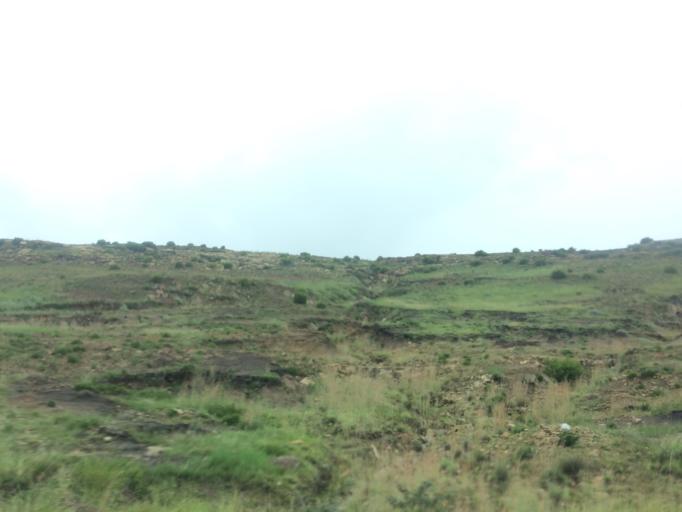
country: LS
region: Maseru
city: Nako
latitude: -29.7561
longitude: 27.5175
